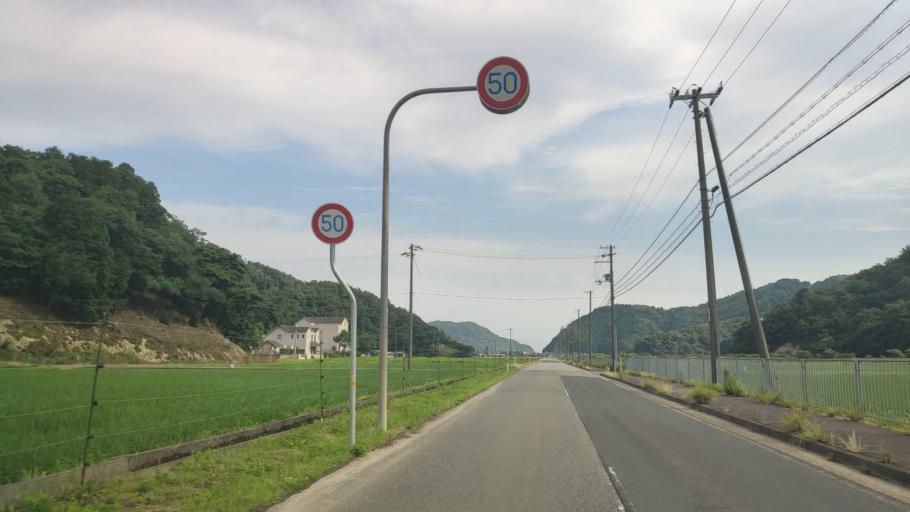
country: JP
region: Hyogo
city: Toyooka
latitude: 35.6242
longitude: 134.8412
